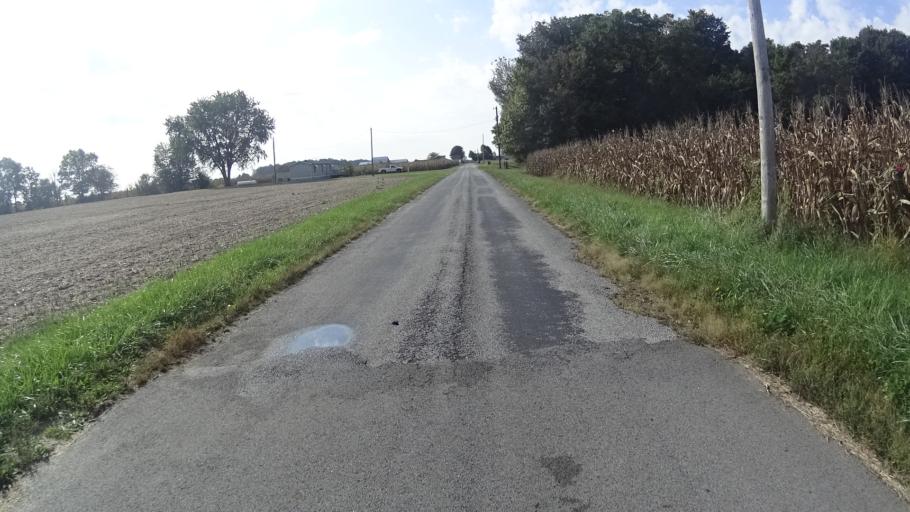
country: US
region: Indiana
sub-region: Madison County
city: Ingalls
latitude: 39.9962
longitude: -85.8243
